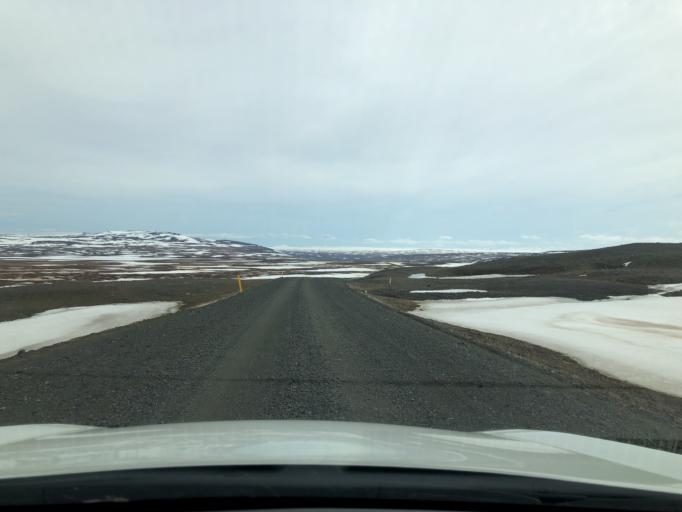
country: IS
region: East
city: Egilsstadir
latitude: 65.3086
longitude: -15.3661
